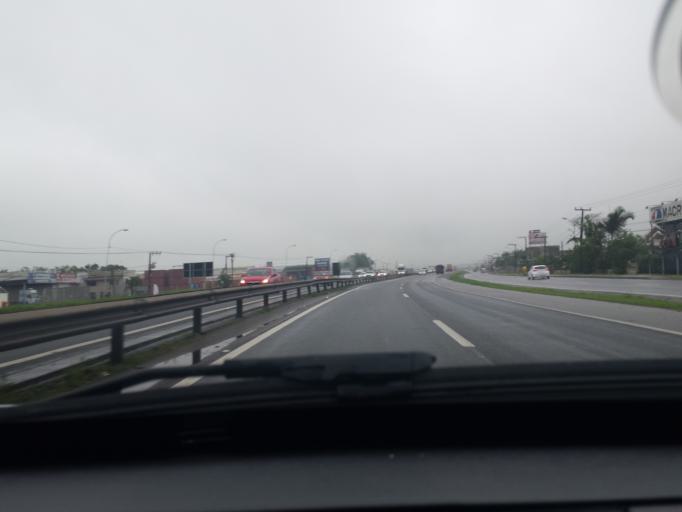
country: BR
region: Santa Catarina
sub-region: Itajai
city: Itajai
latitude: -26.8665
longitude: -48.7300
